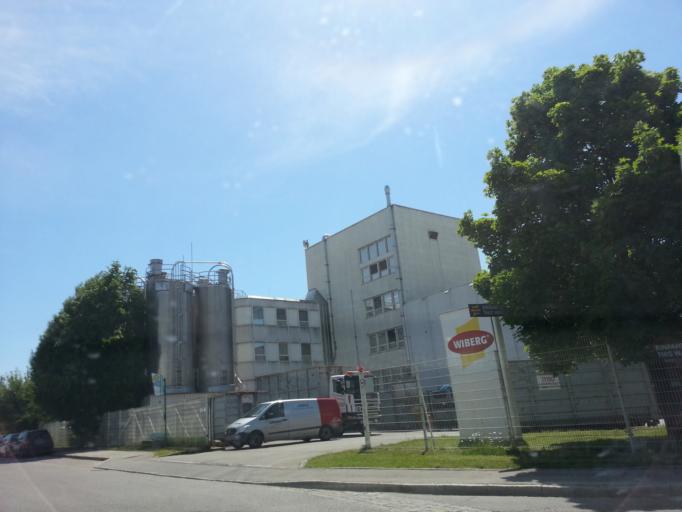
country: DE
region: Bavaria
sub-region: Upper Bavaria
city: Freilassing
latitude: 47.8540
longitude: 12.9621
